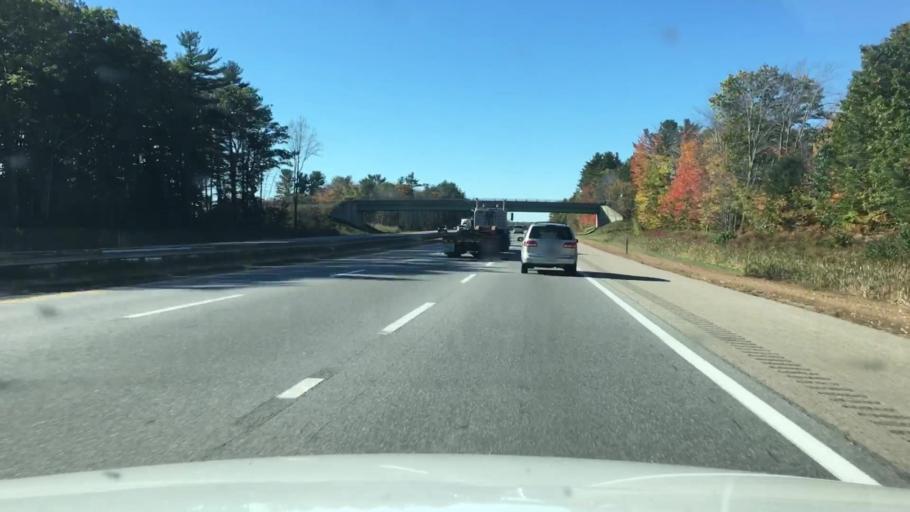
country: US
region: Maine
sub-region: York County
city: Biddeford
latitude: 43.5157
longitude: -70.4688
